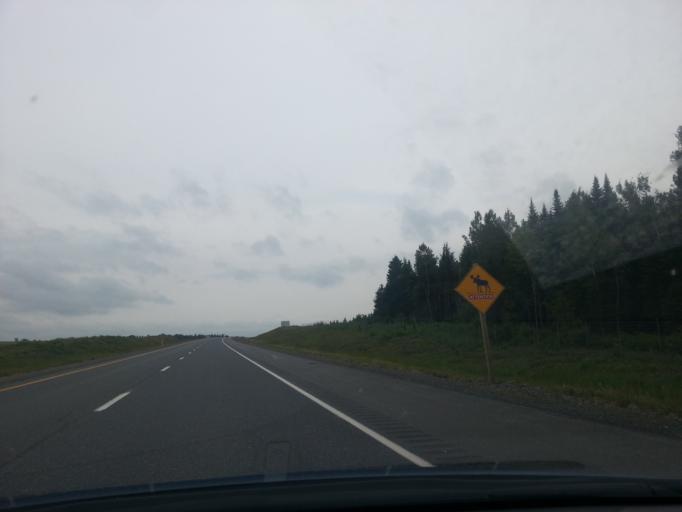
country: CA
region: New Brunswick
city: Florenceville-Bristol
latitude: 46.3317
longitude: -67.6002
